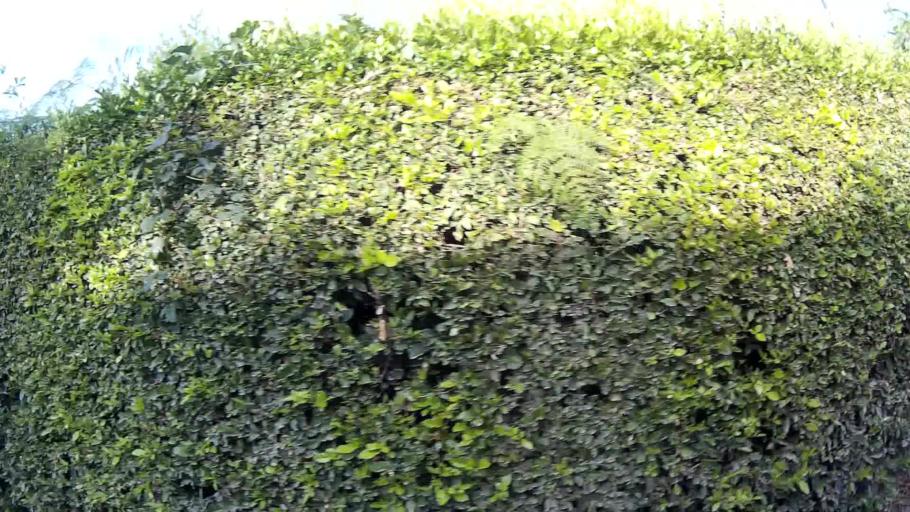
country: CO
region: Valle del Cauca
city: Ulloa
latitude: 4.7339
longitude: -75.7329
